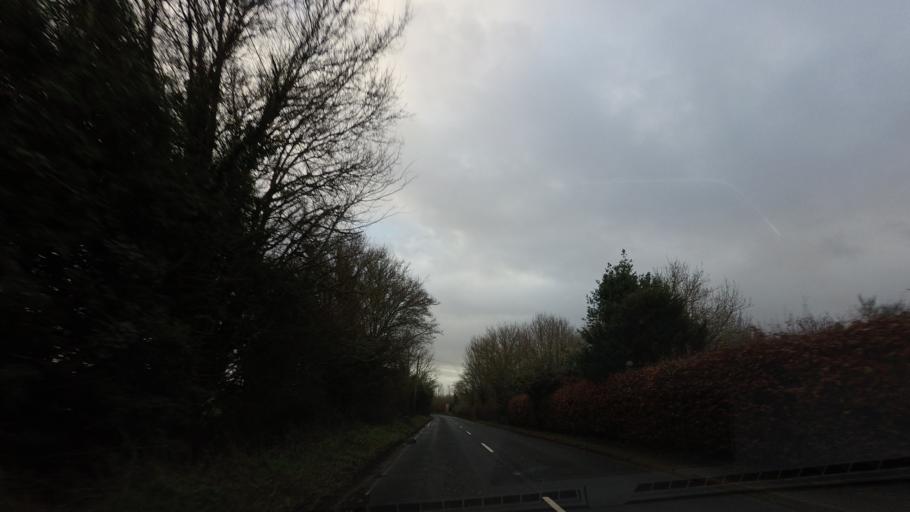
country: GB
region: England
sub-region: Kent
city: Yalding
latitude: 51.2170
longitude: 0.4308
